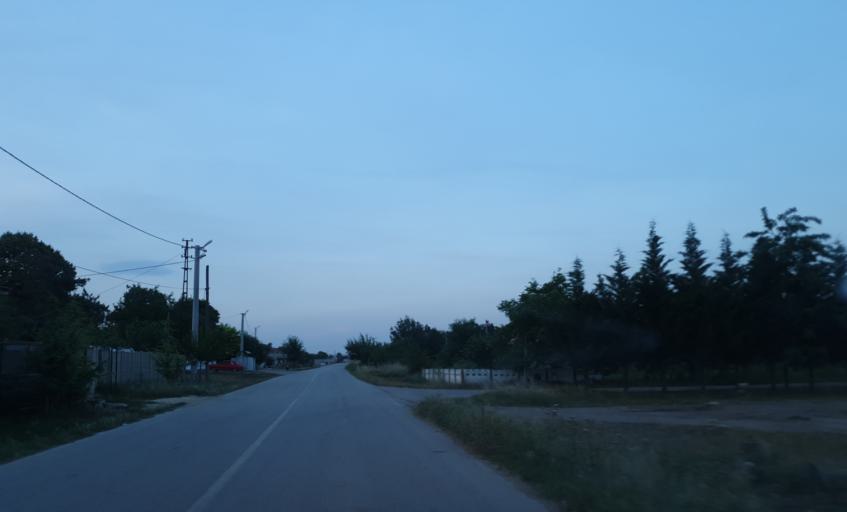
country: TR
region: Tekirdag
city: Beyazkoy
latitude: 41.4372
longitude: 27.6971
